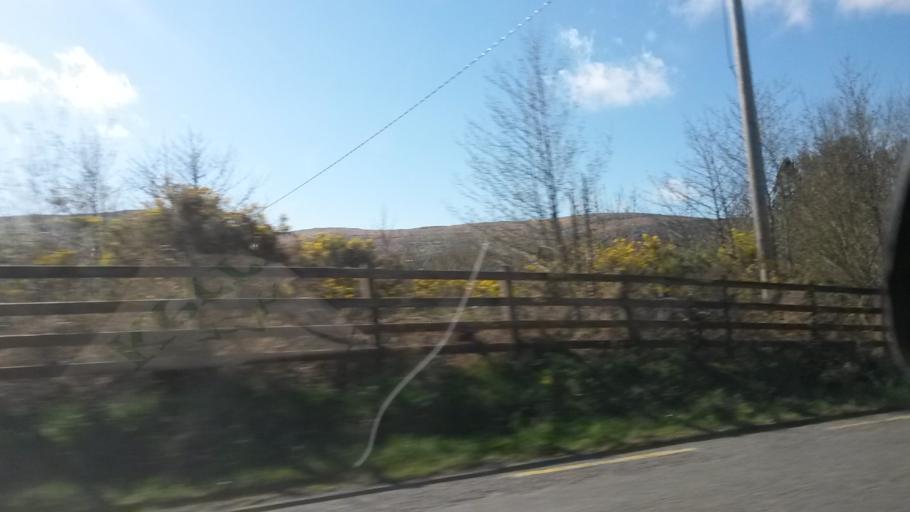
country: IE
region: Munster
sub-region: Ciarrai
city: Cill Airne
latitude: 51.9118
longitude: -9.4039
